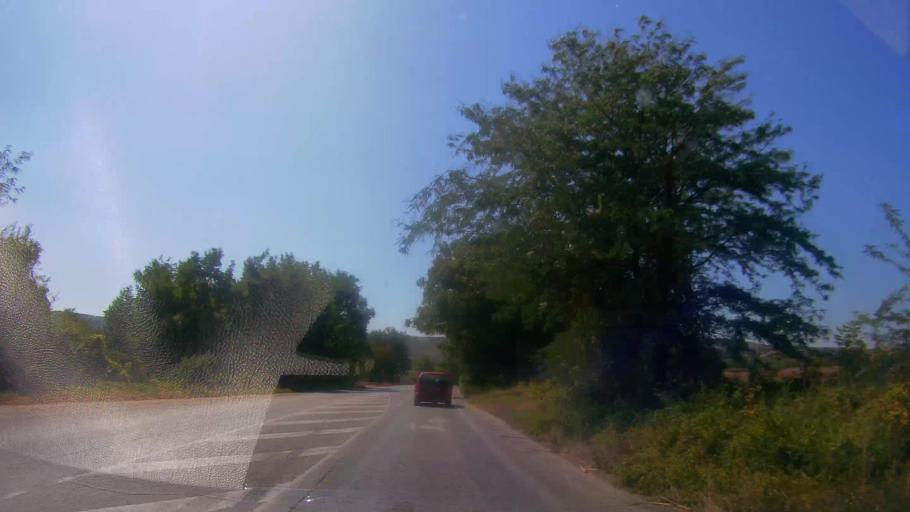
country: BG
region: Veliko Turnovo
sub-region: Obshtina Gorna Oryakhovitsa
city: Purvomaytsi
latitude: 43.1515
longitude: 25.6175
